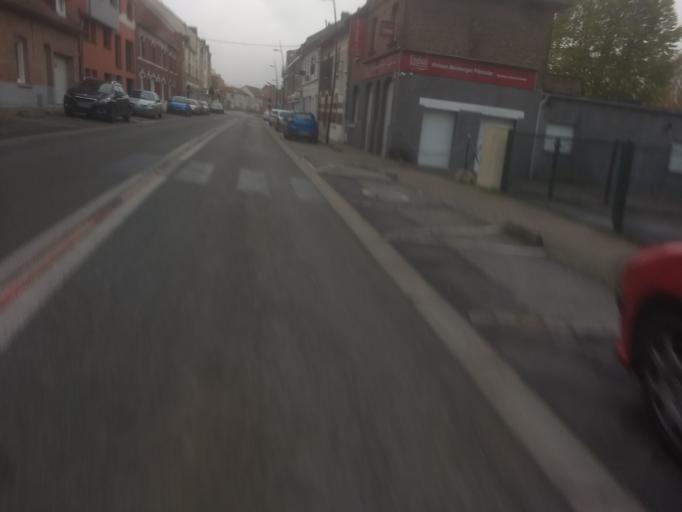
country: FR
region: Nord-Pas-de-Calais
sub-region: Departement du Pas-de-Calais
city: Saint-Laurent-Blangy
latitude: 50.3011
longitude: 2.8036
